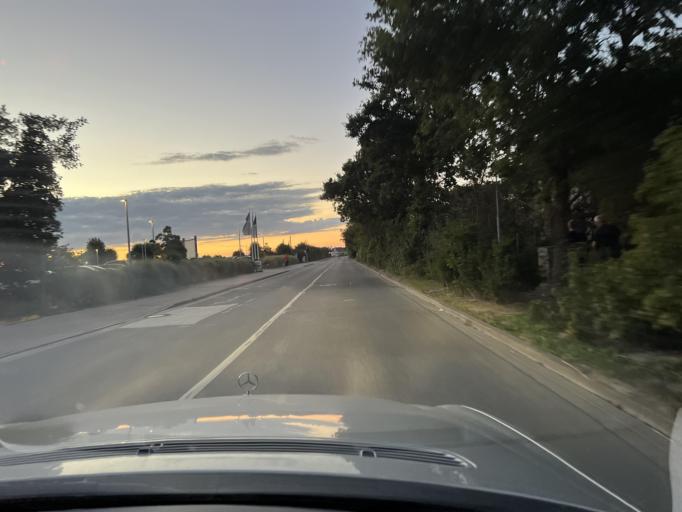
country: DE
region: Schleswig-Holstein
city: Busum
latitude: 54.1362
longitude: 8.8455
